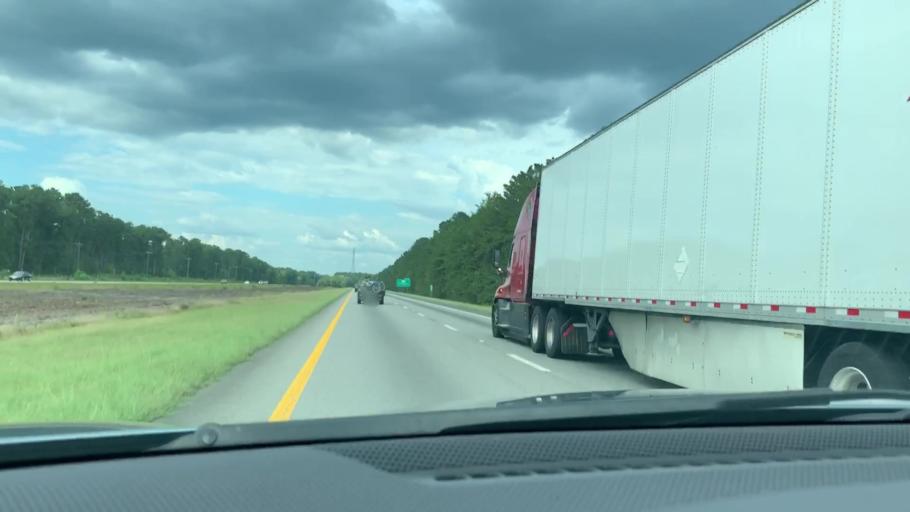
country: US
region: South Carolina
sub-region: Jasper County
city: Ridgeland
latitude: 32.5625
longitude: -80.9423
